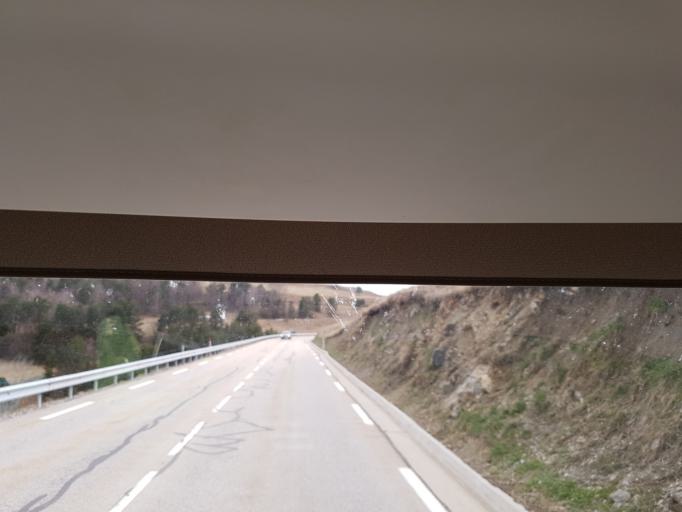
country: FR
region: Languedoc-Roussillon
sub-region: Departement de l'Aude
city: Quillan
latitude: 42.6518
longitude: 2.1232
